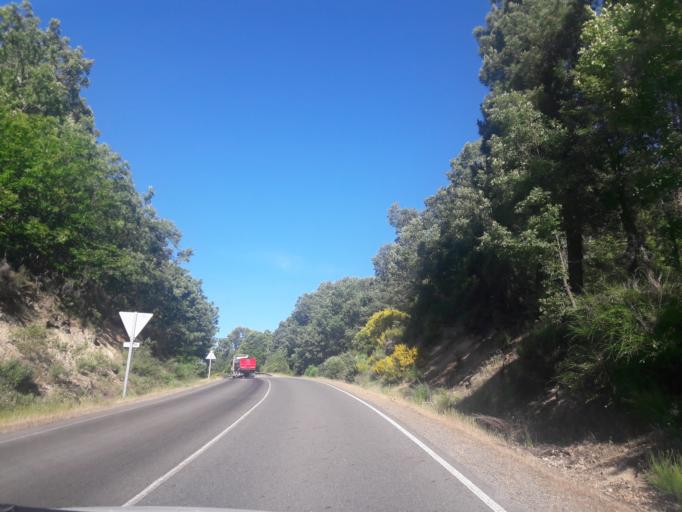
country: ES
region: Castille and Leon
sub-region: Provincia de Salamanca
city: Puerto de Bejar
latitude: 40.3500
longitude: -5.8477
